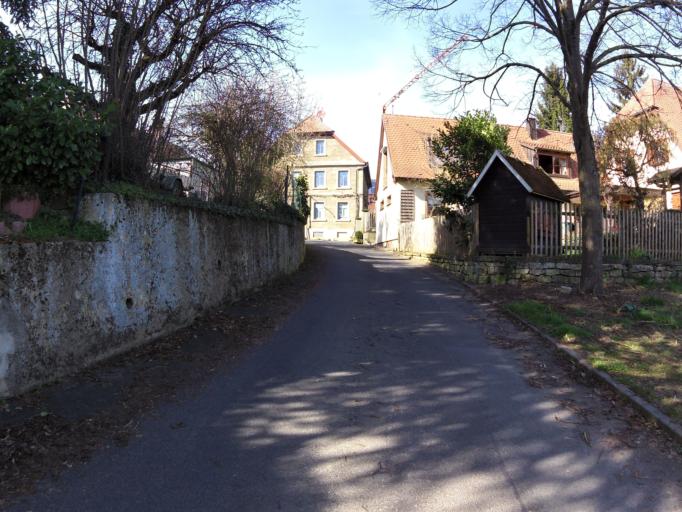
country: DE
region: Bavaria
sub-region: Regierungsbezirk Unterfranken
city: Buchbrunn
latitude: 49.7509
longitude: 10.1238
